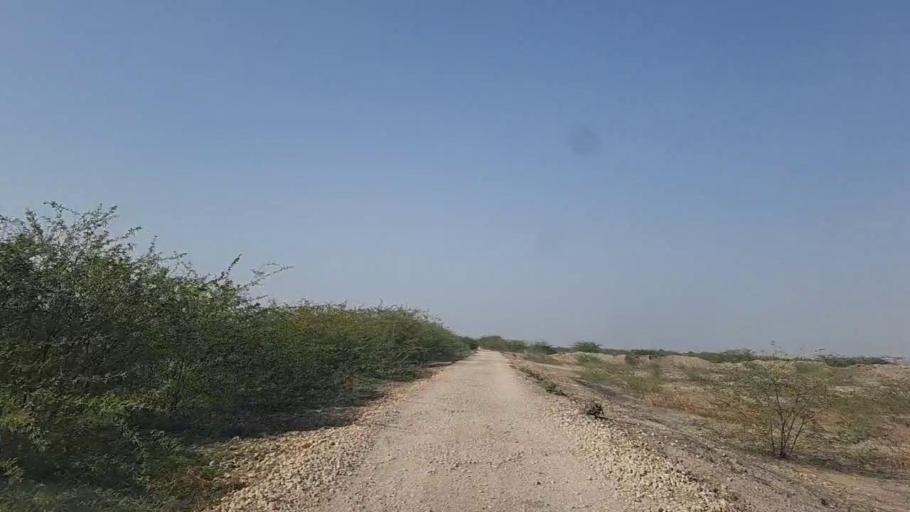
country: PK
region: Sindh
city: Naukot
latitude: 24.6085
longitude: 69.2747
